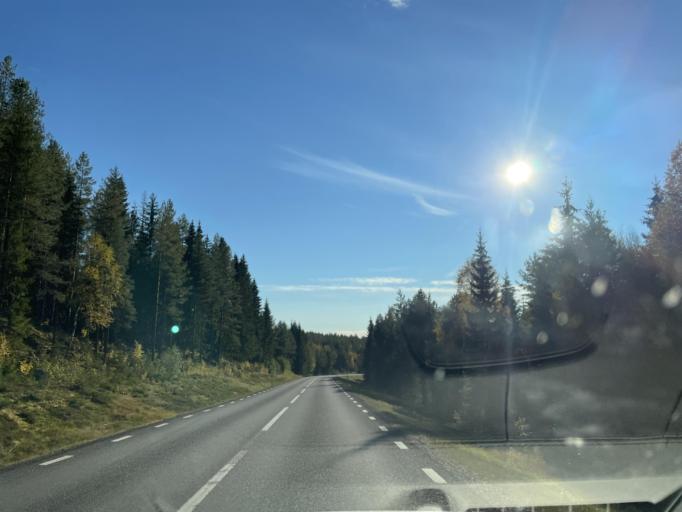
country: SE
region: Vaermland
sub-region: Torsby Kommun
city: Torsby
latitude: 60.3355
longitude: 13.1440
